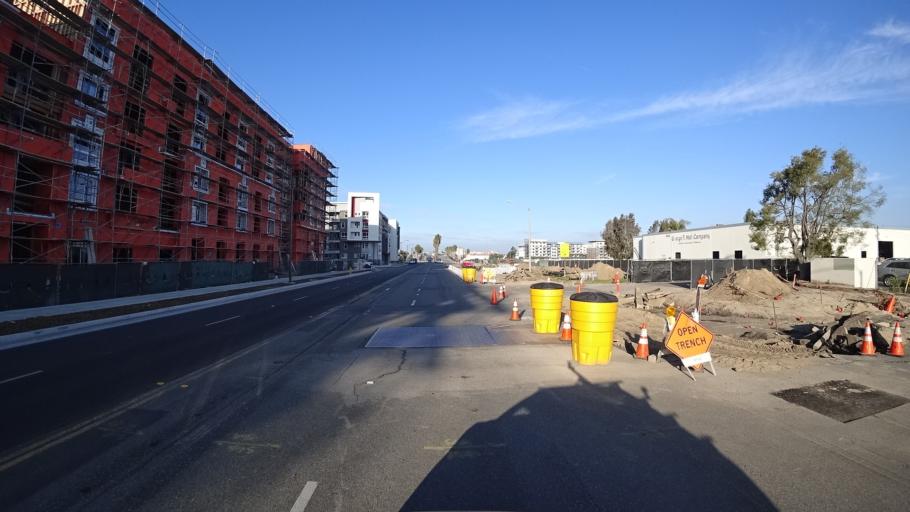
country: US
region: California
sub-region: Orange County
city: Orange
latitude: 33.7994
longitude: -117.8915
